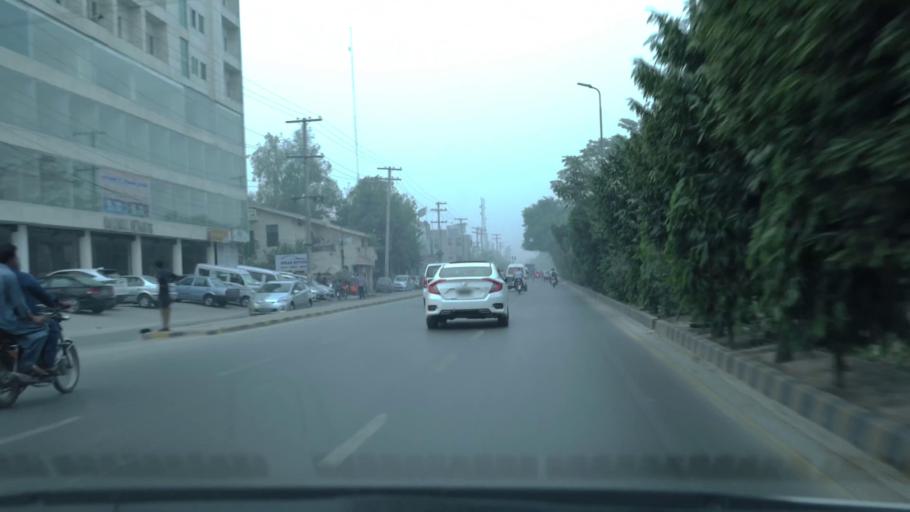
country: PK
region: Punjab
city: Lahore
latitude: 31.4734
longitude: 74.3024
